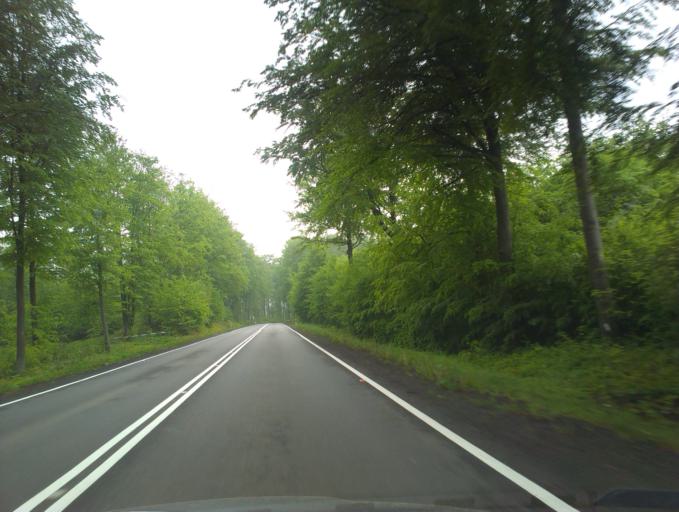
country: PL
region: West Pomeranian Voivodeship
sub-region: Powiat koszalinski
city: Bobolice
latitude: 53.9213
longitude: 16.6030
